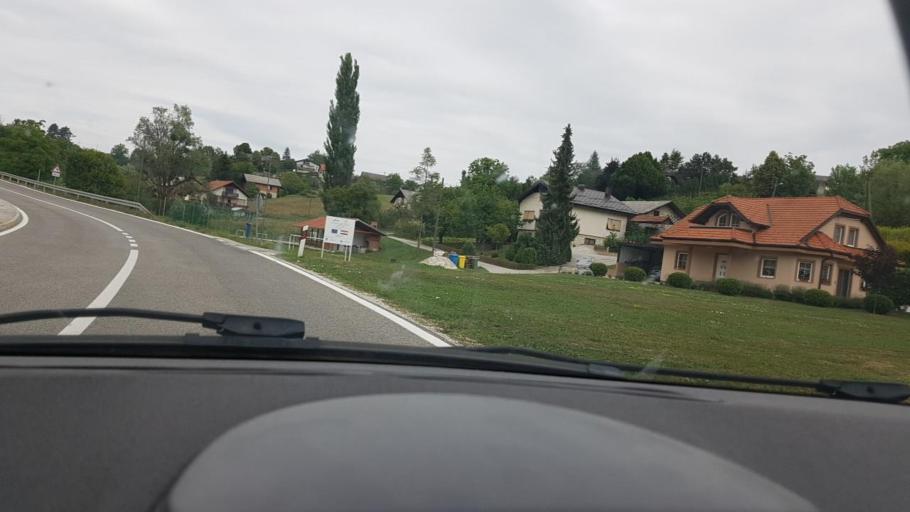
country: SI
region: Rogatec
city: Rogatec
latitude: 46.2076
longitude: 15.6900
